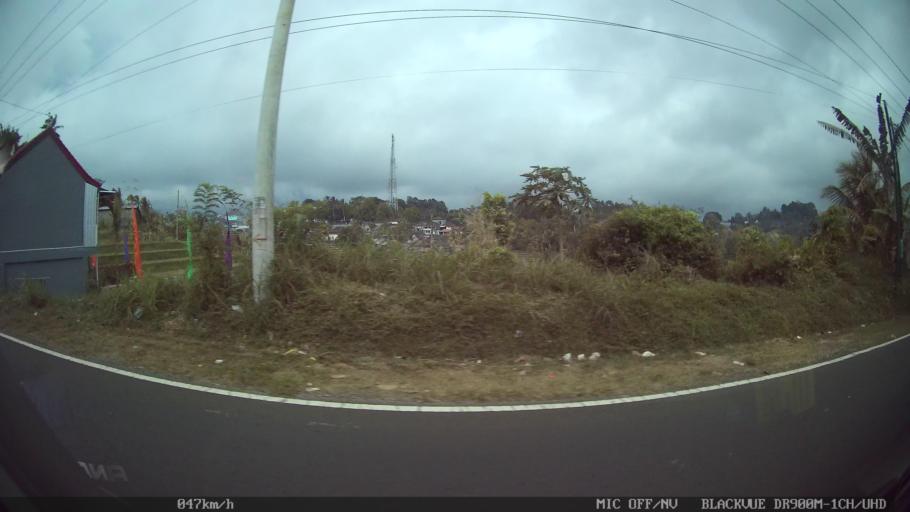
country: ID
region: Bali
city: Bantiran
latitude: -8.3134
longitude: 114.9999
